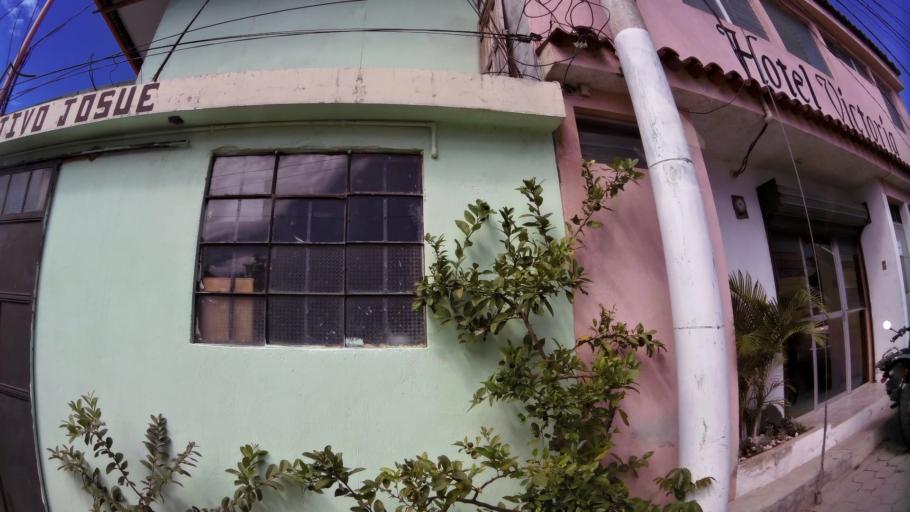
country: GT
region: Solola
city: Panajachel
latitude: 14.7431
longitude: -91.1526
